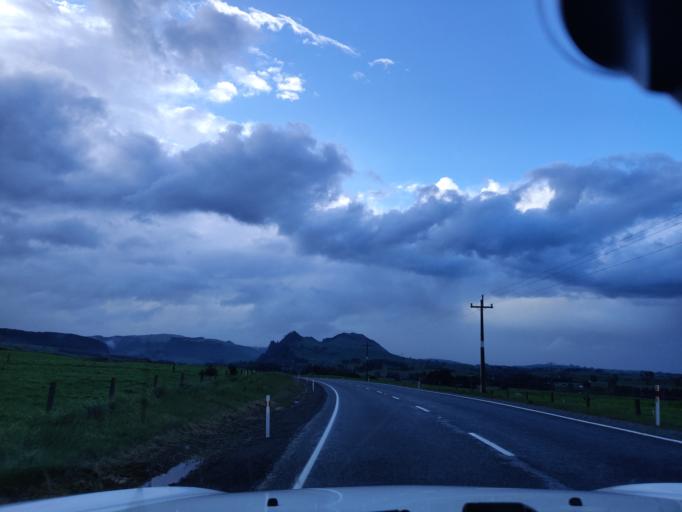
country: NZ
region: Waikato
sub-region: South Waikato District
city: Tokoroa
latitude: -38.4024
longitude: 175.7905
